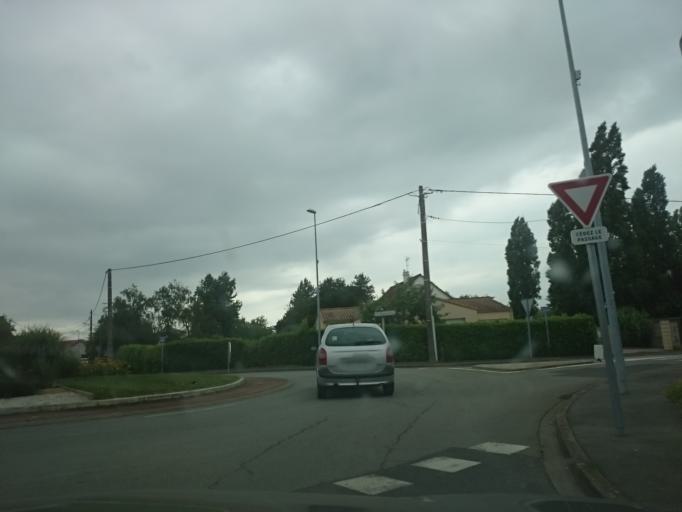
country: FR
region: Pays de la Loire
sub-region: Departement de la Loire-Atlantique
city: Saint-Jean-de-Boiseau
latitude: 47.1913
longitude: -1.7073
